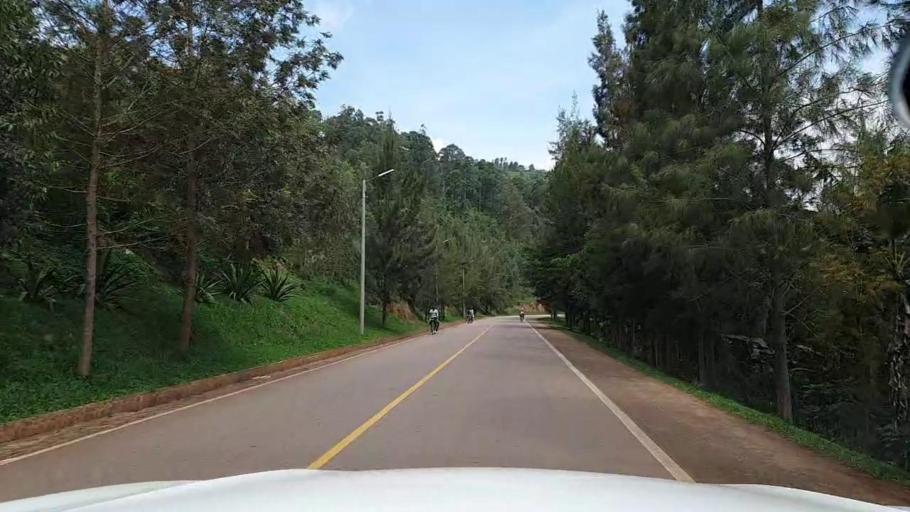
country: RW
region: Kigali
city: Kigali
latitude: -1.8639
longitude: 30.0881
